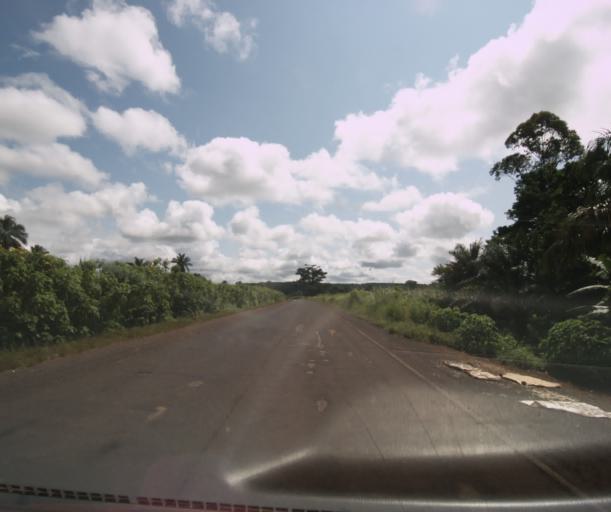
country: CM
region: West
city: Foumban
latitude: 5.6908
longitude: 10.8089
